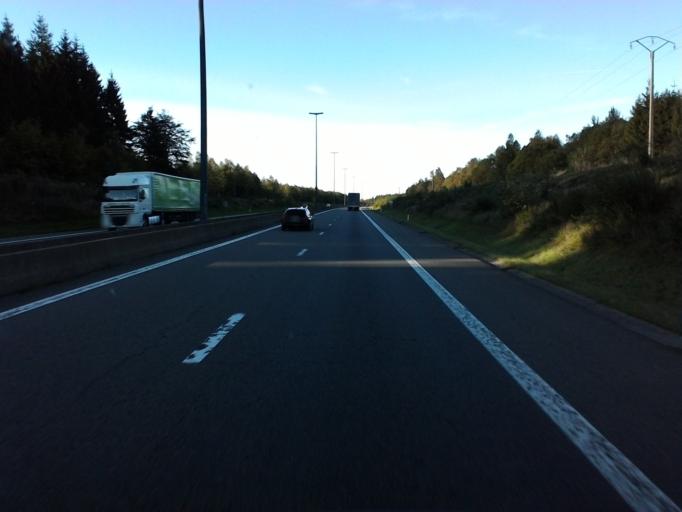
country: BE
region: Wallonia
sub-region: Province de Liege
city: Lierneux
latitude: 50.2187
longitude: 5.7730
